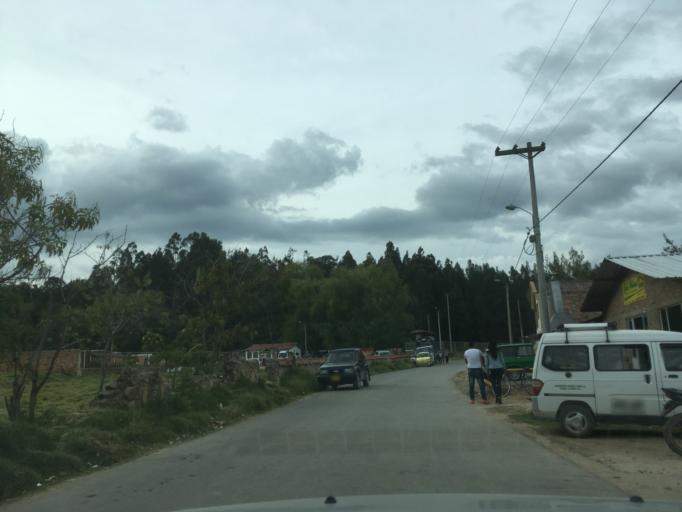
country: CO
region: Boyaca
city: Firavitoba
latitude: 5.6747
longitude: -73.0040
